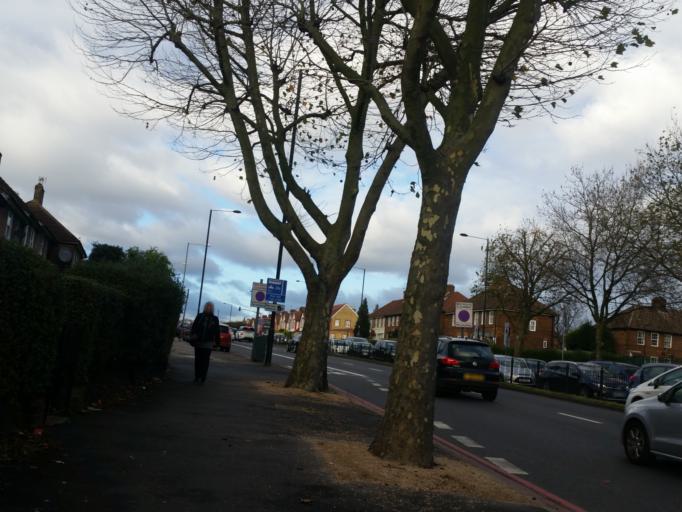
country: GB
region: England
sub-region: Greater London
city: Harringay
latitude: 51.6058
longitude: -0.0862
